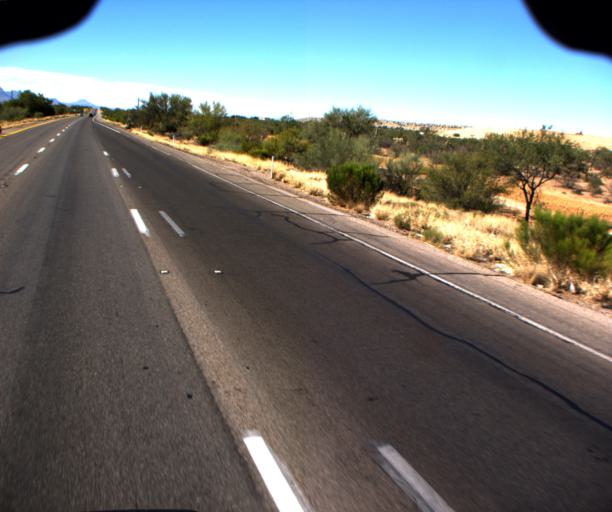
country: US
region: Arizona
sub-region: Pima County
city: Sahuarita
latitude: 31.9527
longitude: -110.9874
